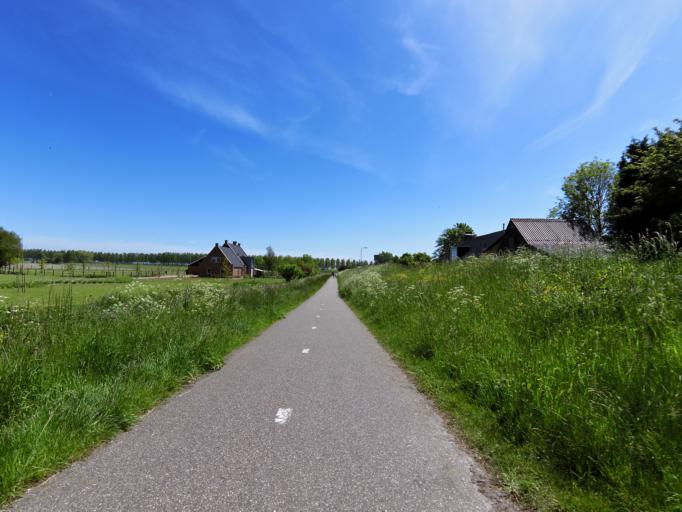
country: NL
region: South Holland
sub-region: Gemeente Hellevoetsluis
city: Nieuw-Helvoet
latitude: 51.8543
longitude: 4.0874
